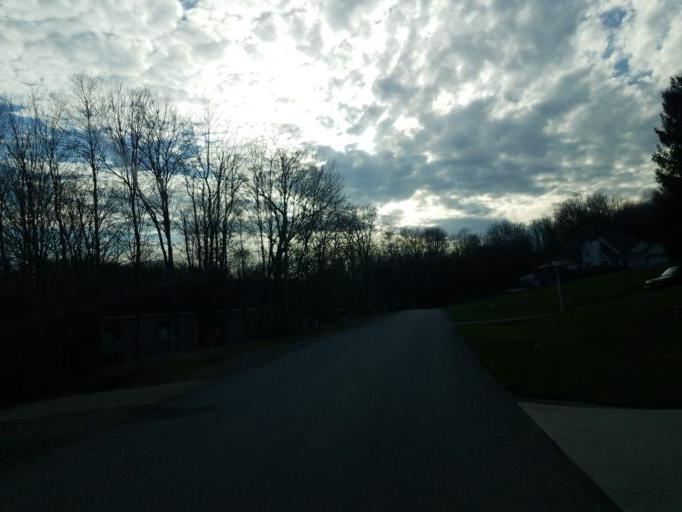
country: US
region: Ohio
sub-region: Knox County
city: Gambier
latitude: 40.4262
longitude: -82.3507
